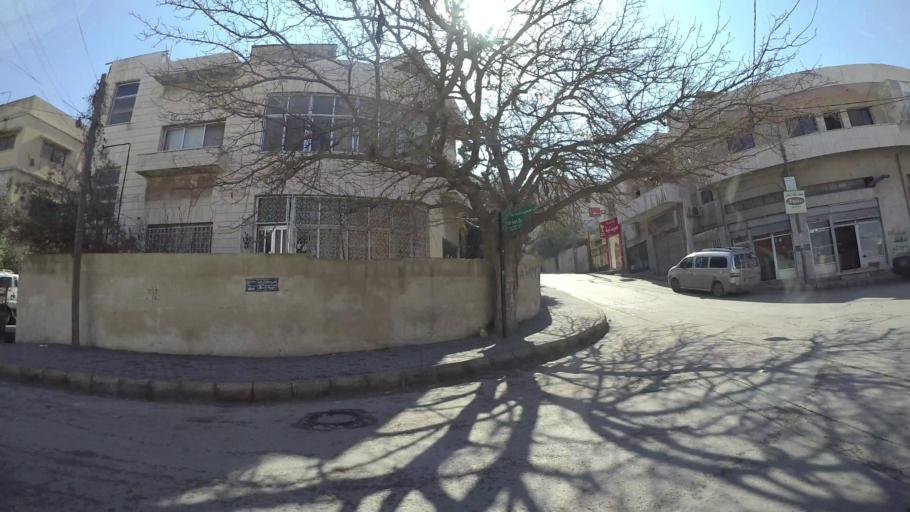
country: JO
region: Amman
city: Amman
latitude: 31.9850
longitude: 35.9876
